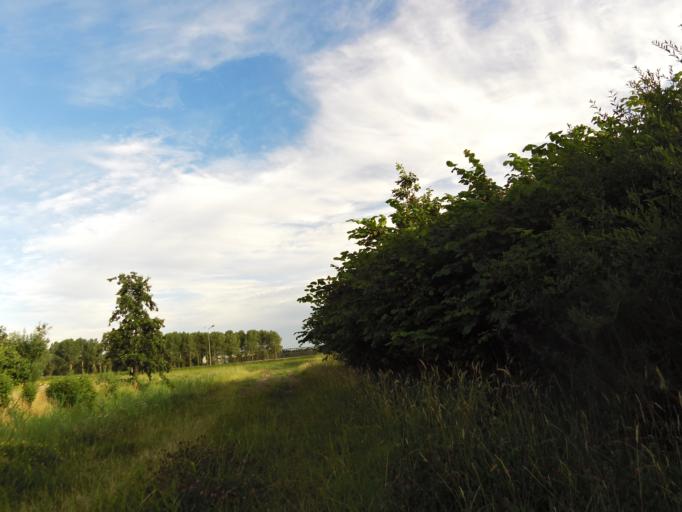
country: NL
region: South Holland
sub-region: Gemeente Noordwijk
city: Noordwijk-Binnen
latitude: 52.2141
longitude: 4.4373
